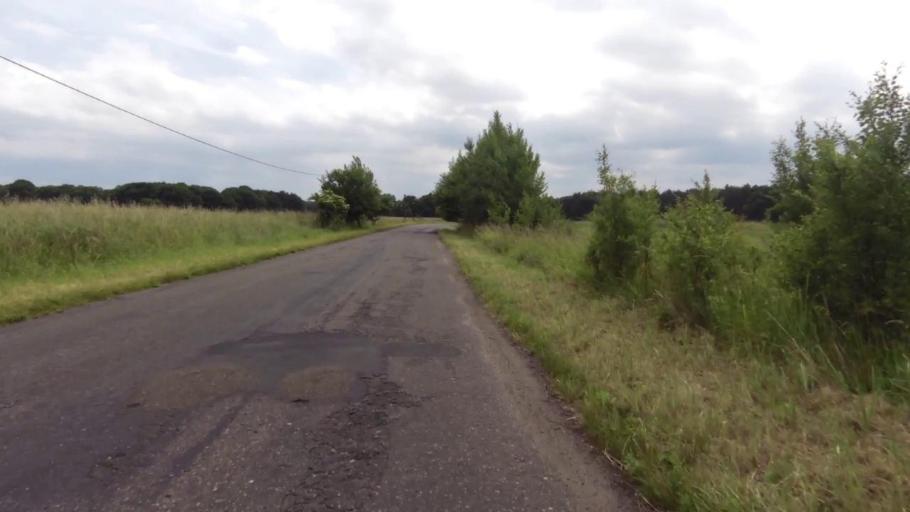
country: PL
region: West Pomeranian Voivodeship
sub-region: Powiat goleniowski
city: Stepnica
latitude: 53.7162
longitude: 14.5546
